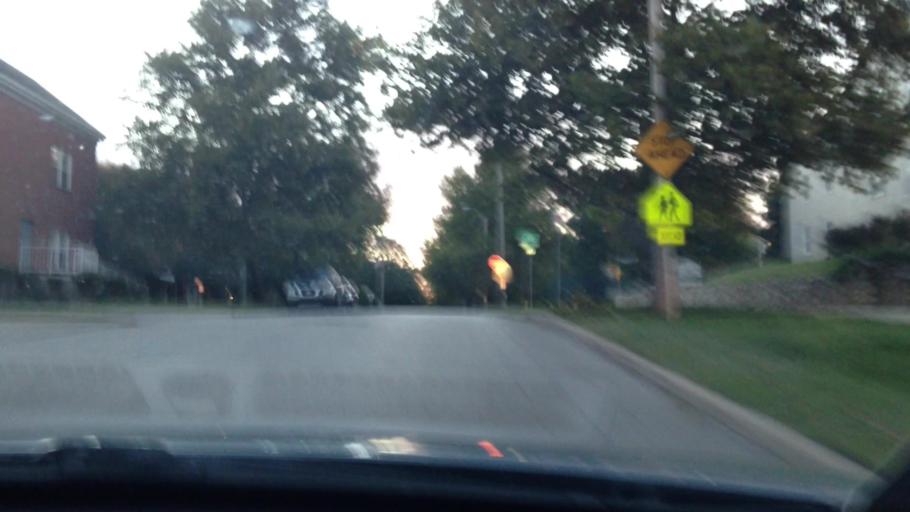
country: US
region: Missouri
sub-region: Jackson County
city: Kansas City
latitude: 39.0619
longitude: -94.5826
